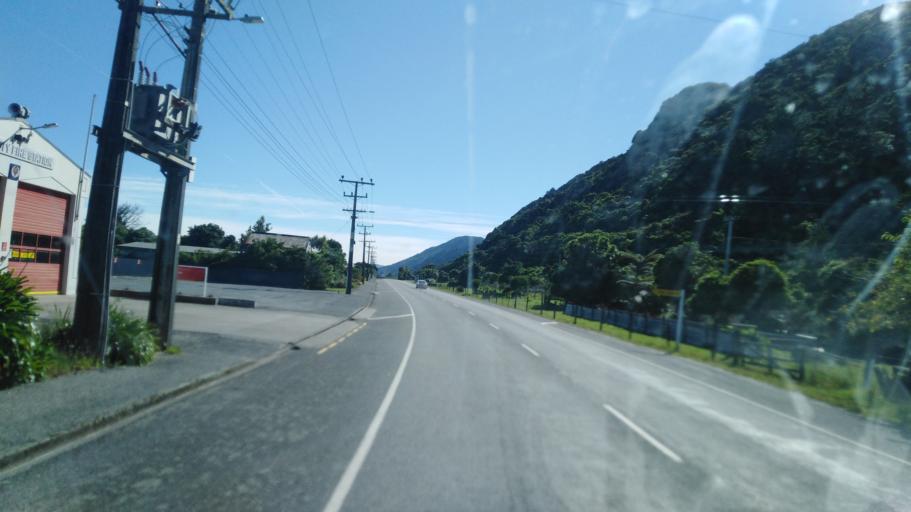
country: NZ
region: West Coast
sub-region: Buller District
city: Westport
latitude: -41.6280
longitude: 171.8552
